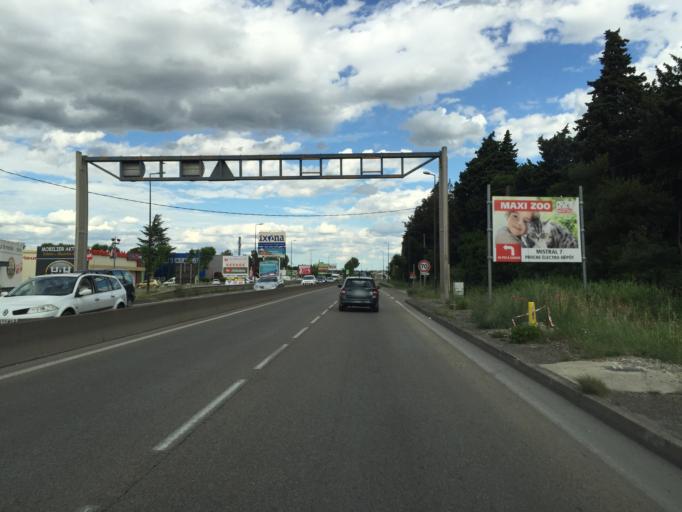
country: FR
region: Provence-Alpes-Cote d'Azur
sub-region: Departement du Vaucluse
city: Montfavet
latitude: 43.9245
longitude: 4.8507
